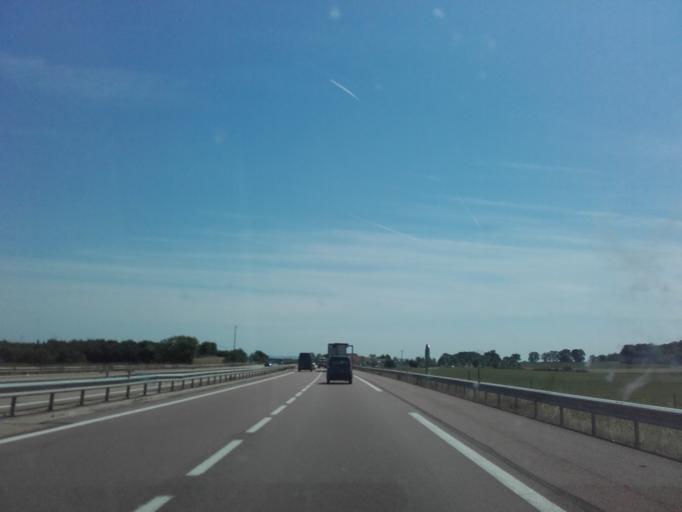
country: FR
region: Bourgogne
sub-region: Departement de l'Yonne
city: Avallon
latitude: 47.5033
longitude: 4.0288
